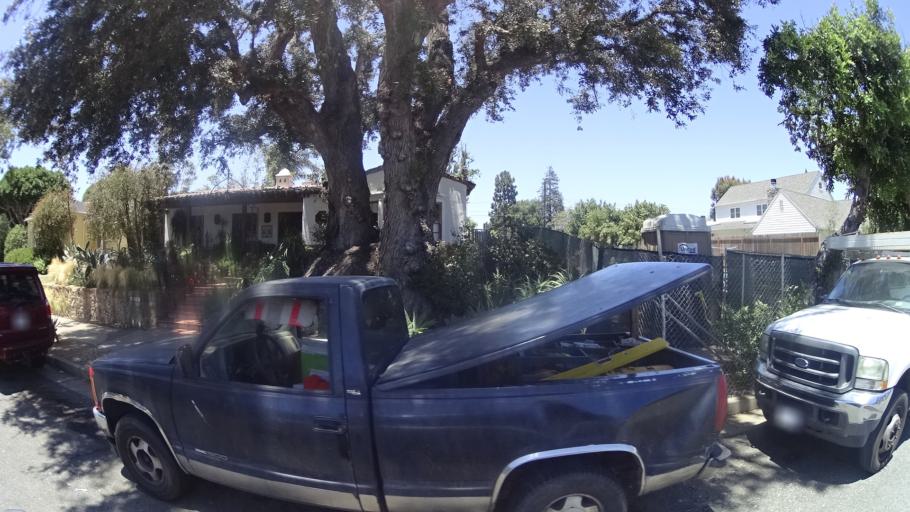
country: US
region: California
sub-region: Los Angeles County
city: Santa Monica
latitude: 34.0092
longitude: -118.4683
